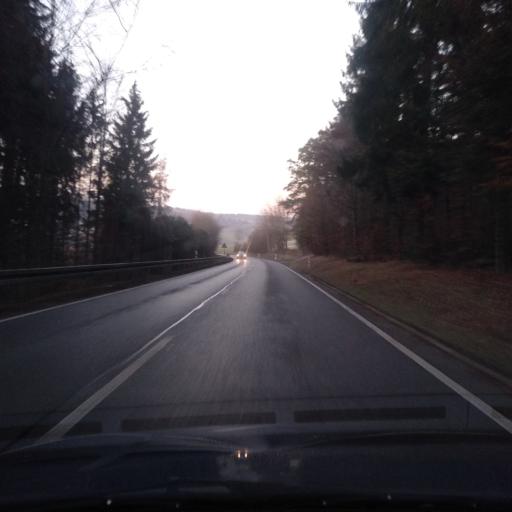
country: DE
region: Baden-Wuerttemberg
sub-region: Karlsruhe Region
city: Calw
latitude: 48.6877
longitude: 8.7720
